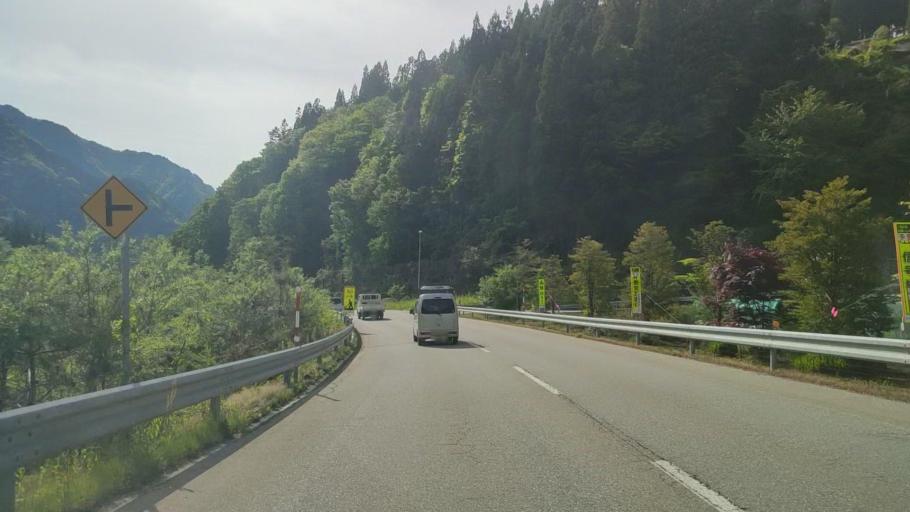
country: JP
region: Gifu
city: Takayama
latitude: 36.2695
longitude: 137.4046
